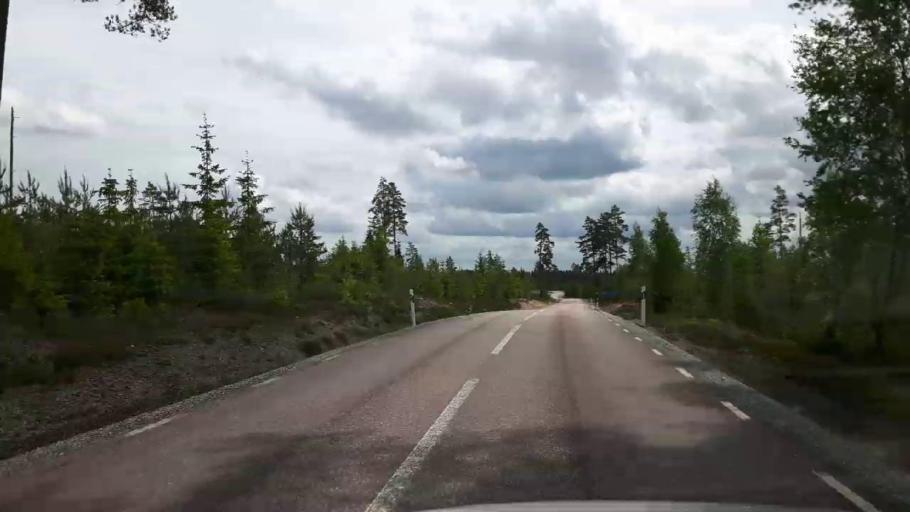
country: SE
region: Vaestmanland
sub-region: Fagersta Kommun
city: Fagersta
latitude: 59.8934
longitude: 15.8223
